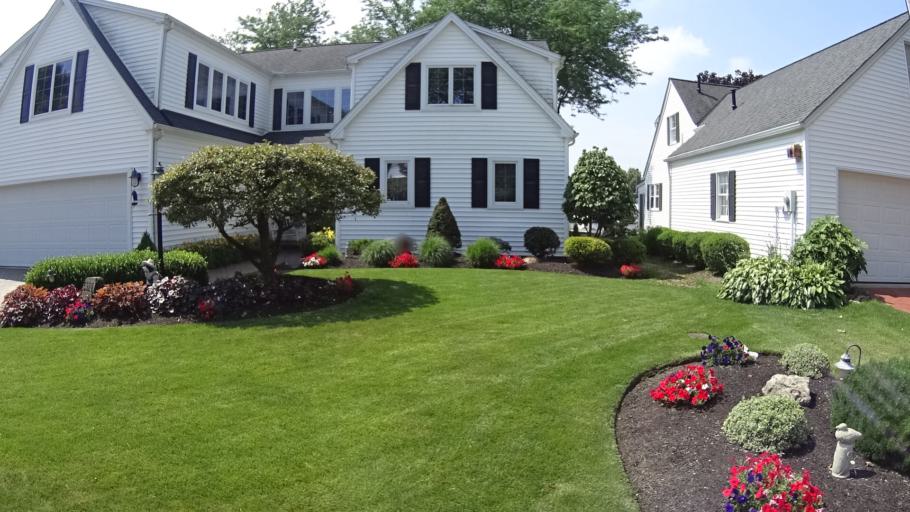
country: US
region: Ohio
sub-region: Lorain County
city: Vermilion
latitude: 41.4236
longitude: -82.3612
